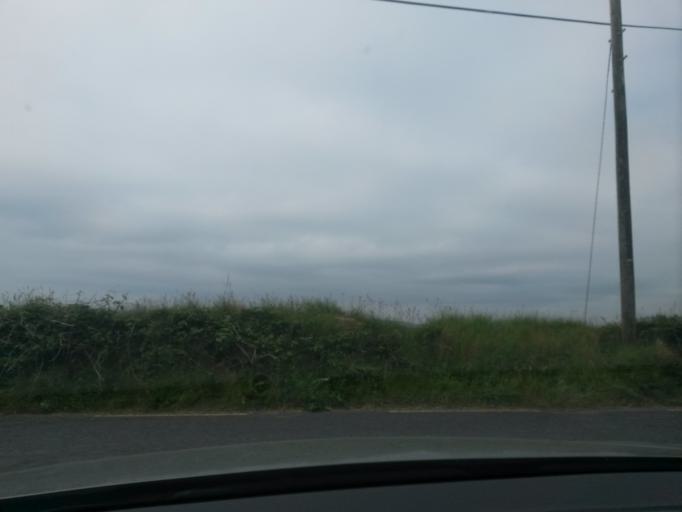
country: IE
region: Munster
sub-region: Ciarrai
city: Ballybunnion
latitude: 52.5341
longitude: -9.6669
